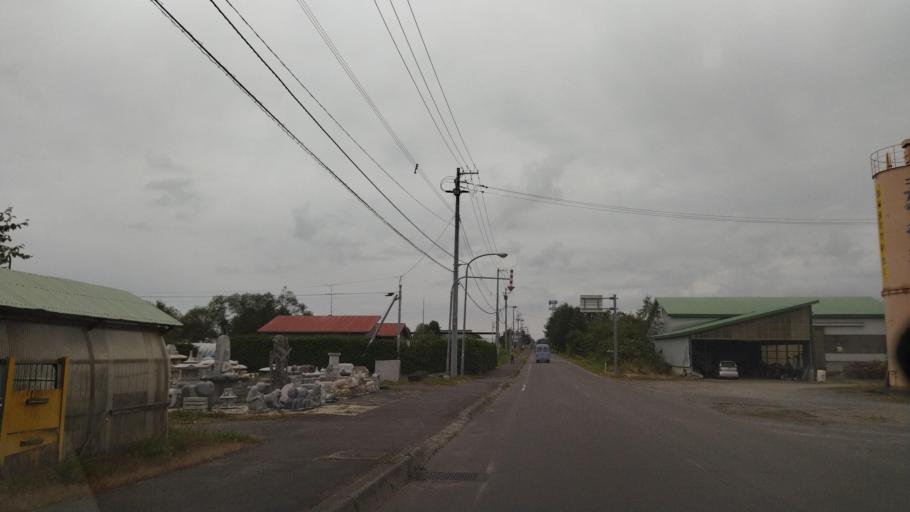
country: JP
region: Hokkaido
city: Otofuke
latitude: 43.2266
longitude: 143.2799
